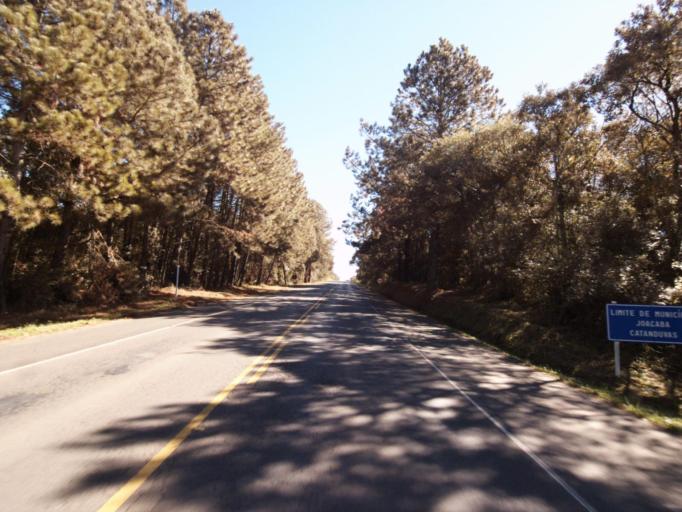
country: BR
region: Santa Catarina
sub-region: Joacaba
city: Joacaba
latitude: -27.1064
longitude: -51.6428
